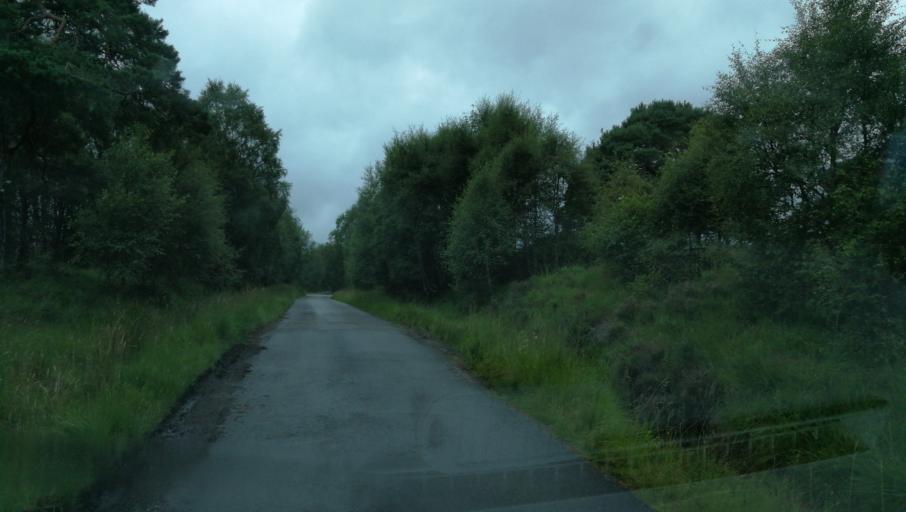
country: GB
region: Scotland
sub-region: Highland
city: Spean Bridge
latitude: 57.2675
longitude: -4.9740
